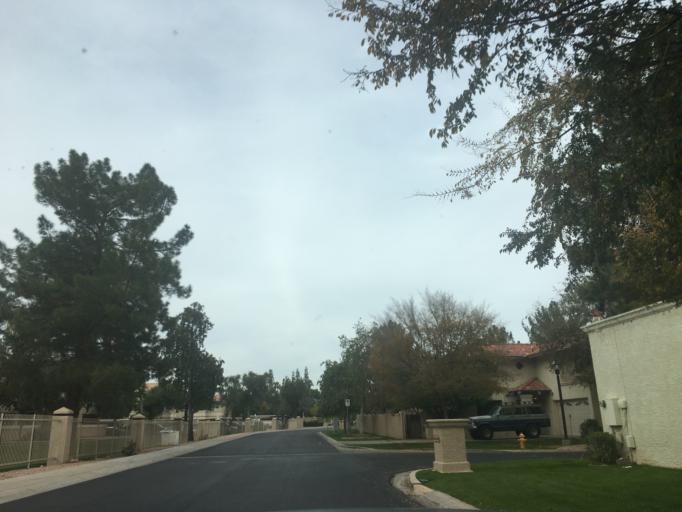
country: US
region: Arizona
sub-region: Maricopa County
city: Gilbert
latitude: 33.3622
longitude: -111.7864
